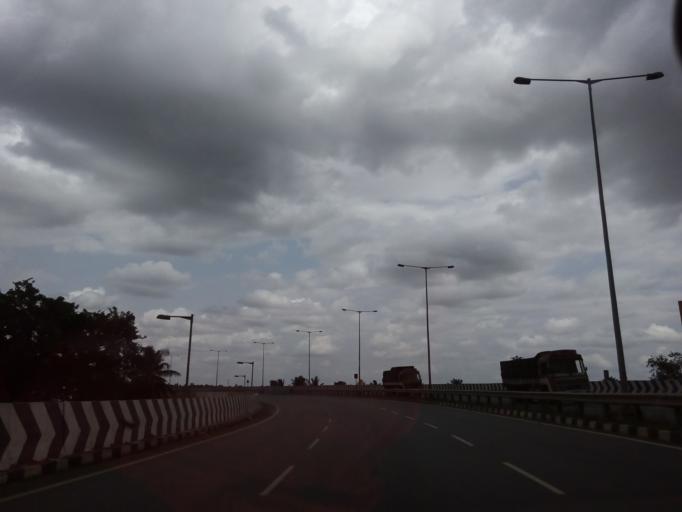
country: IN
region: Karnataka
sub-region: Chitradurga
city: Hiriyur
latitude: 13.9588
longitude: 76.6122
